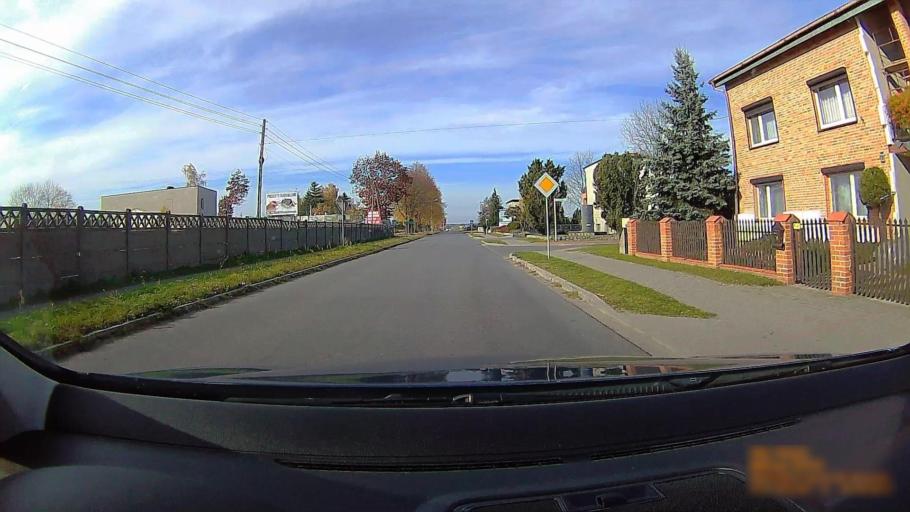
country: PL
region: Greater Poland Voivodeship
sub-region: Powiat ostrzeszowski
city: Doruchow
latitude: 51.4175
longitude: 18.0740
